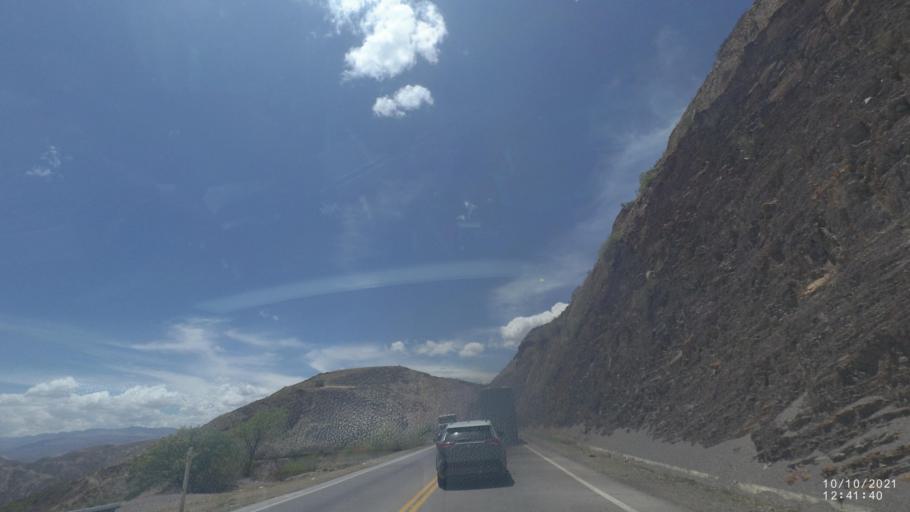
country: BO
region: Cochabamba
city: Irpa Irpa
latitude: -17.6343
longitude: -66.3907
